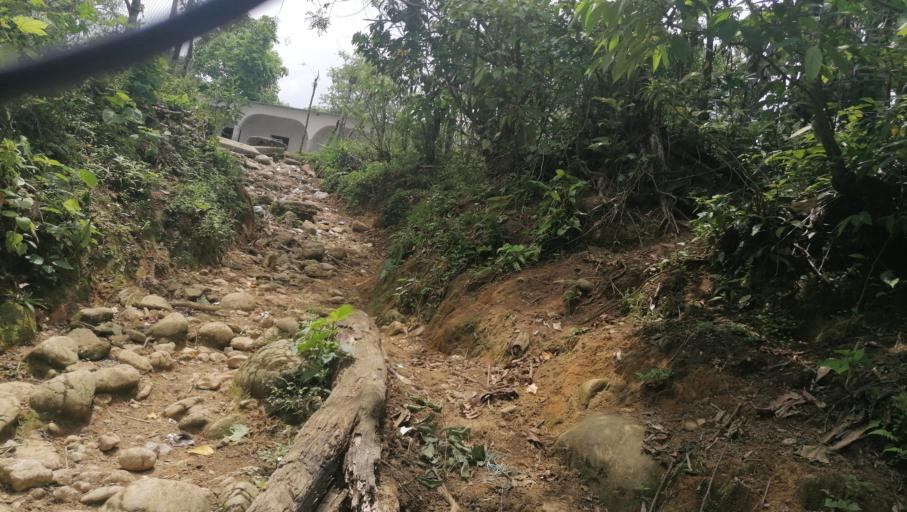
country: MX
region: Chiapas
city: Ocotepec
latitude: 17.2902
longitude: -93.2221
